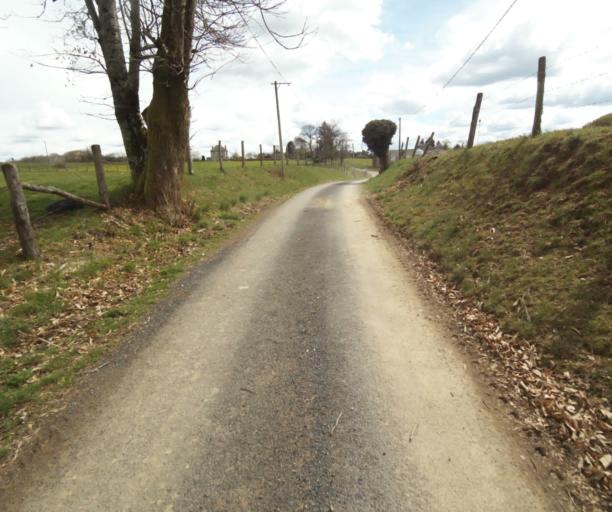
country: FR
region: Limousin
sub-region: Departement de la Correze
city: Laguenne
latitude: 45.2055
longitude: 1.8783
